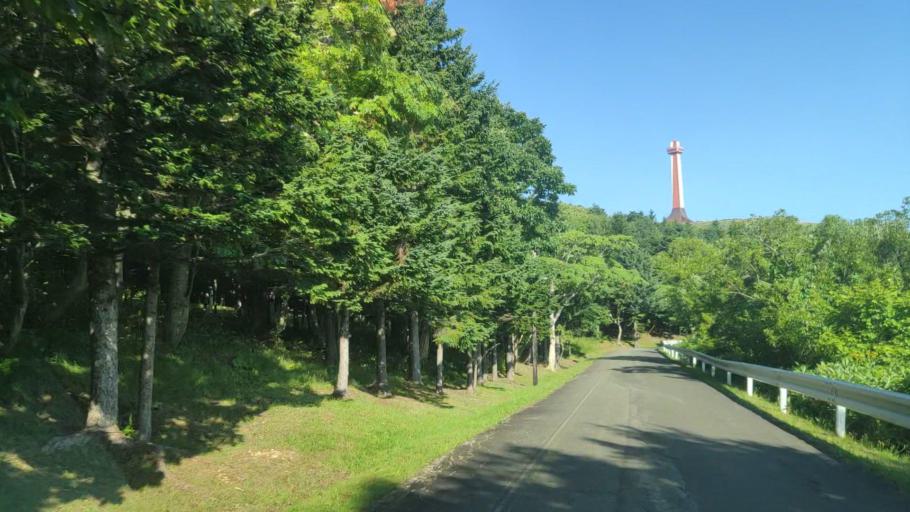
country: JP
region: Hokkaido
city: Wakkanai
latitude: 45.4129
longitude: 141.6694
